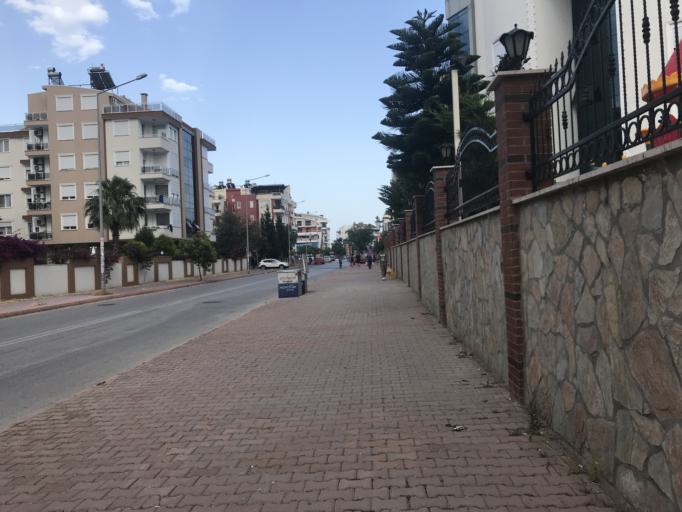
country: TR
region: Antalya
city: Cakirlar
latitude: 36.8497
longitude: 30.6116
